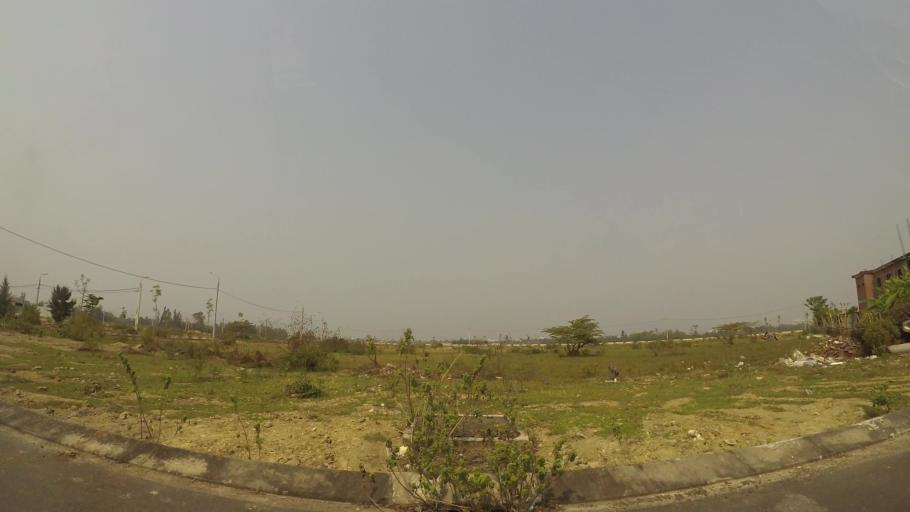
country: VN
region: Da Nang
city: Ngu Hanh Son
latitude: 15.9866
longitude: 108.2277
